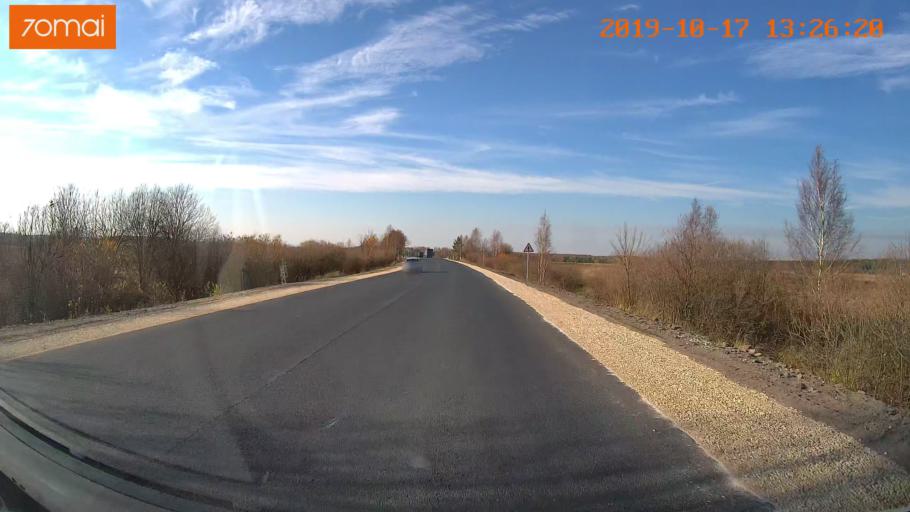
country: RU
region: Rjazan
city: Gus'-Zheleznyy
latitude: 55.1095
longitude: 40.9237
